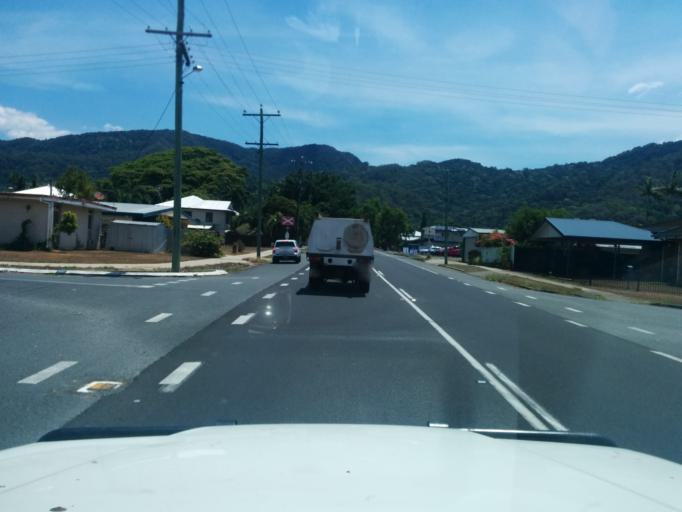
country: AU
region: Queensland
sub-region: Cairns
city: Woree
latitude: -16.9436
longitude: 145.7356
